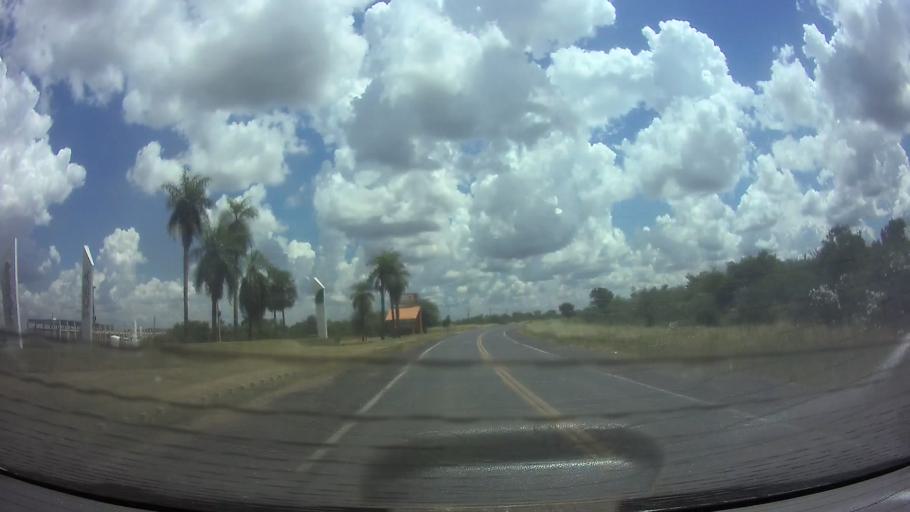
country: PY
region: Central
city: Colonia Mariano Roque Alonso
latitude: -25.1870
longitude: -57.5958
